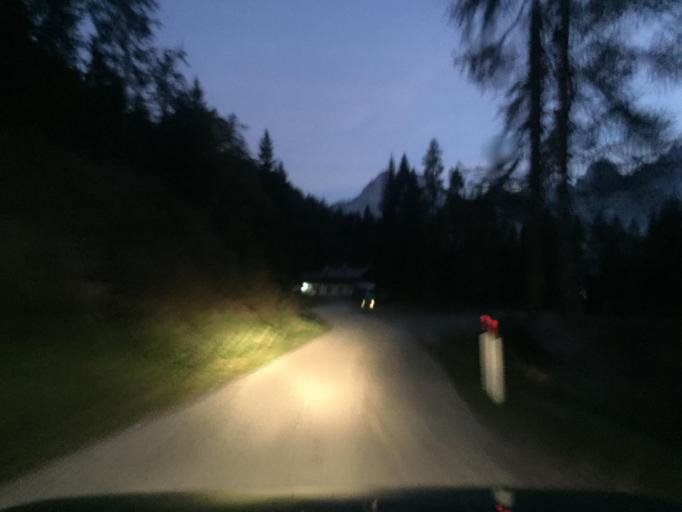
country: IT
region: Veneto
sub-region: Provincia di Belluno
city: Granvilla
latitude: 46.5867
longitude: 12.7270
